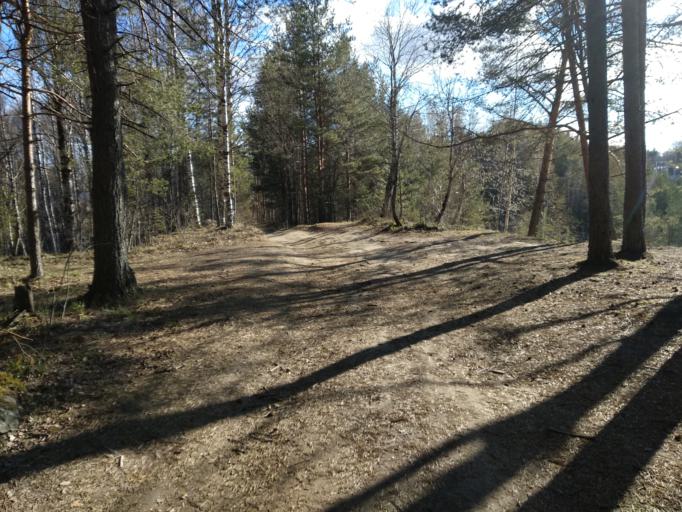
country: RU
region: Republic of Karelia
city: Girvas
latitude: 62.4848
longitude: 33.6788
